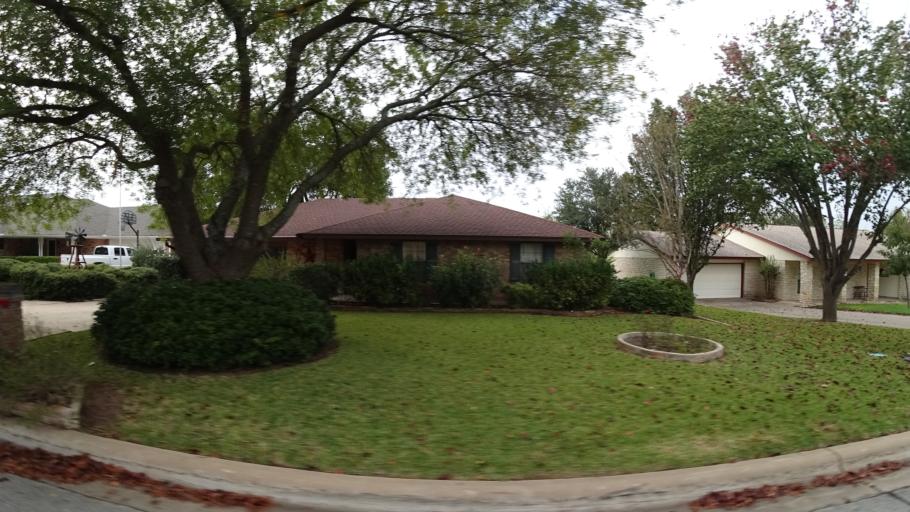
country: US
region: Texas
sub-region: Williamson County
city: Round Rock
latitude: 30.4992
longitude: -97.6949
